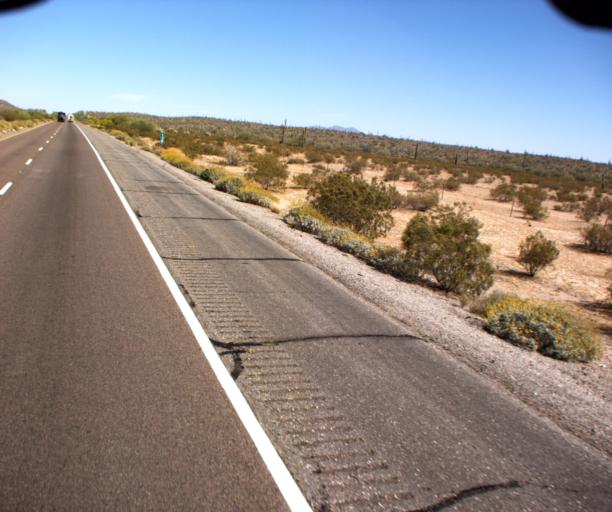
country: US
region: Arizona
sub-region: Pinal County
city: Maricopa
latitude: 32.8502
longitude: -112.3509
